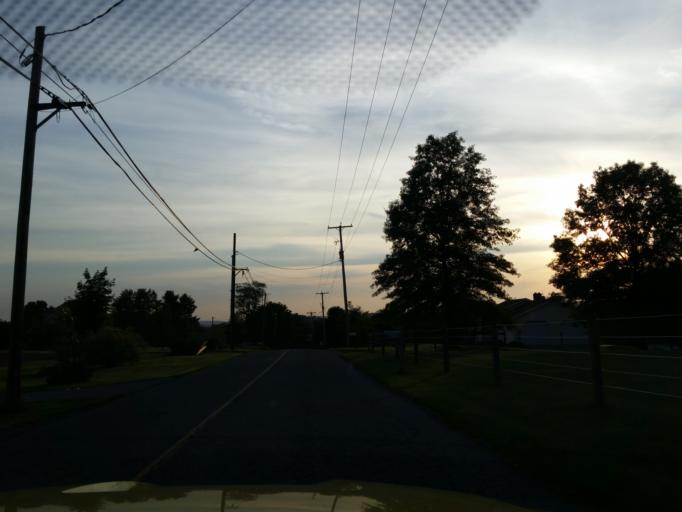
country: US
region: Pennsylvania
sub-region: Lebanon County
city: Fredericksburg
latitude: 40.4482
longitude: -76.3819
